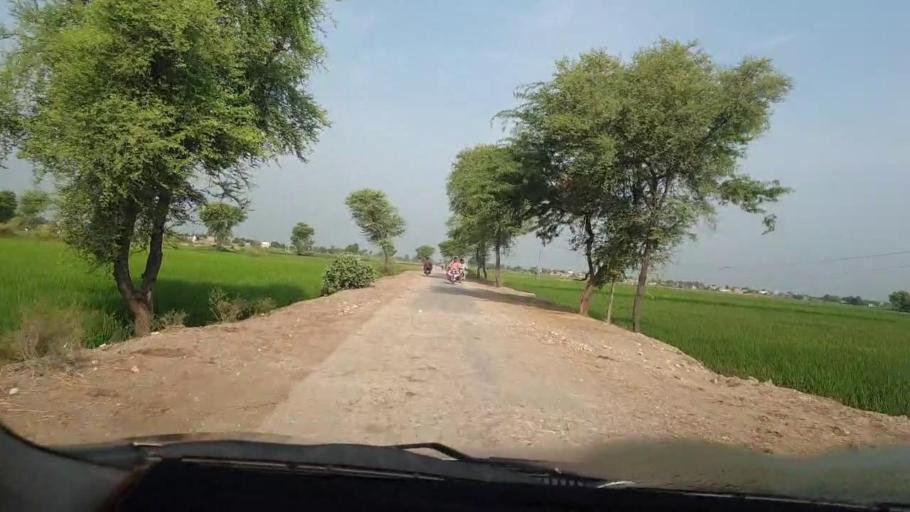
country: PK
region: Sindh
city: Goth Garelo
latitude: 27.4831
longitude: 68.0750
